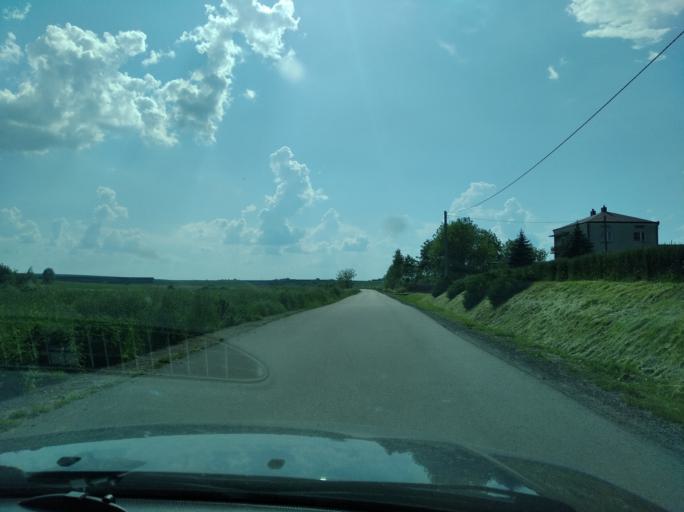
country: PL
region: Subcarpathian Voivodeship
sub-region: Powiat jaroslawski
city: Ostrow
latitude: 49.9274
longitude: 22.7385
